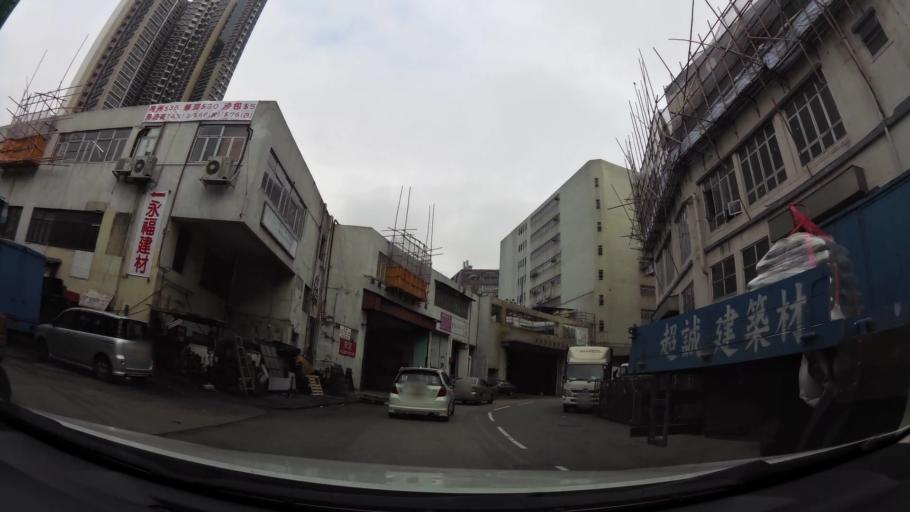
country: HK
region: Kowloon City
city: Kowloon
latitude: 22.2940
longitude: 114.2356
